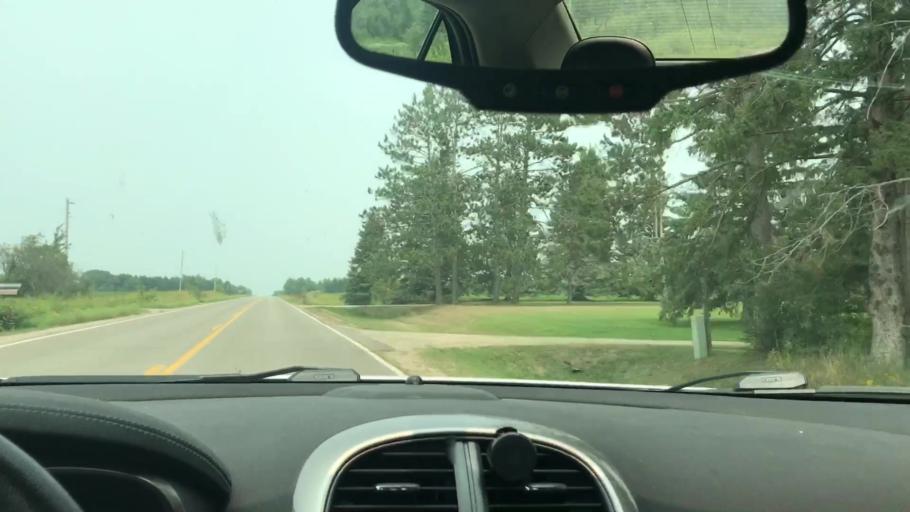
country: US
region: Minnesota
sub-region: Itasca County
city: Cohasset
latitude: 47.3754
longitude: -93.8802
